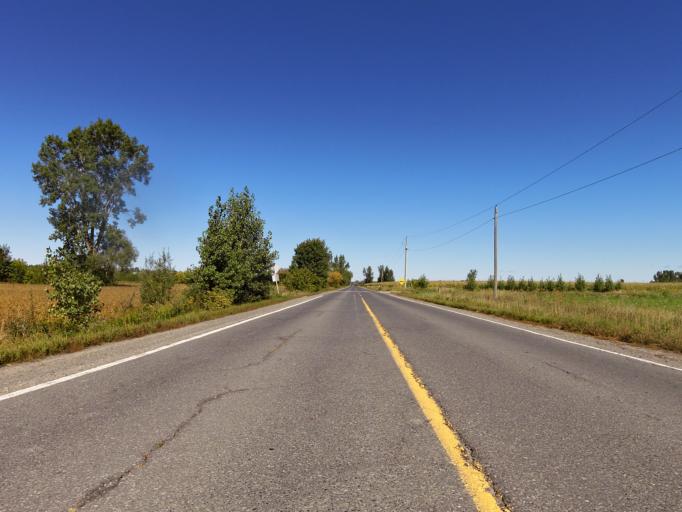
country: CA
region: Ontario
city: Clarence-Rockland
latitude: 45.3205
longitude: -75.4114
